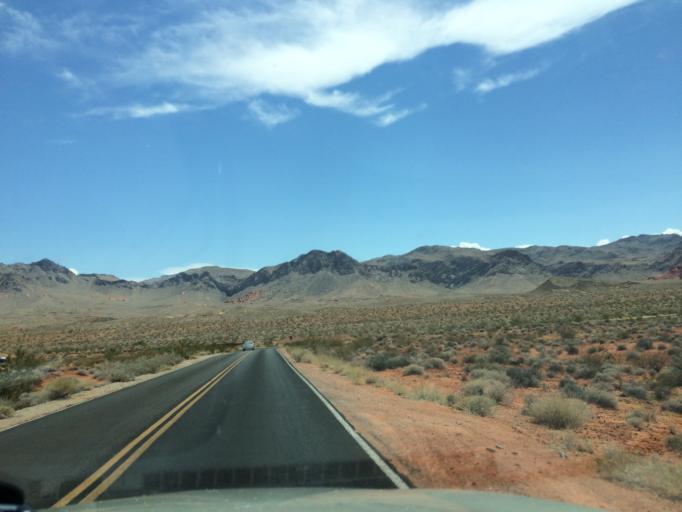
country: US
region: Nevada
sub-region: Clark County
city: Moapa Valley
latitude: 36.4278
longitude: -114.5136
